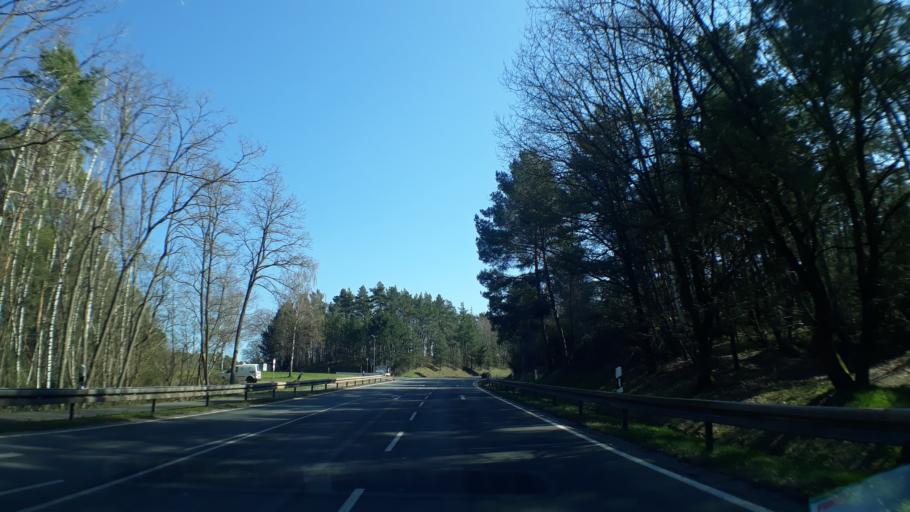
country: DE
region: North Rhine-Westphalia
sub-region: Regierungsbezirk Koln
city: Mechernich
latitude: 50.5842
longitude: 6.6513
